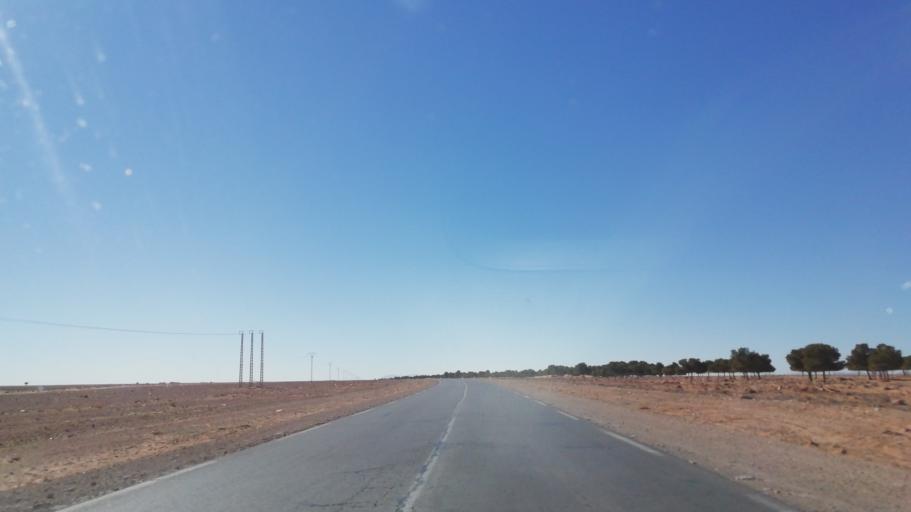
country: DZ
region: Saida
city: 'Ain el Hadjar
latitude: 34.0026
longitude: 0.0450
